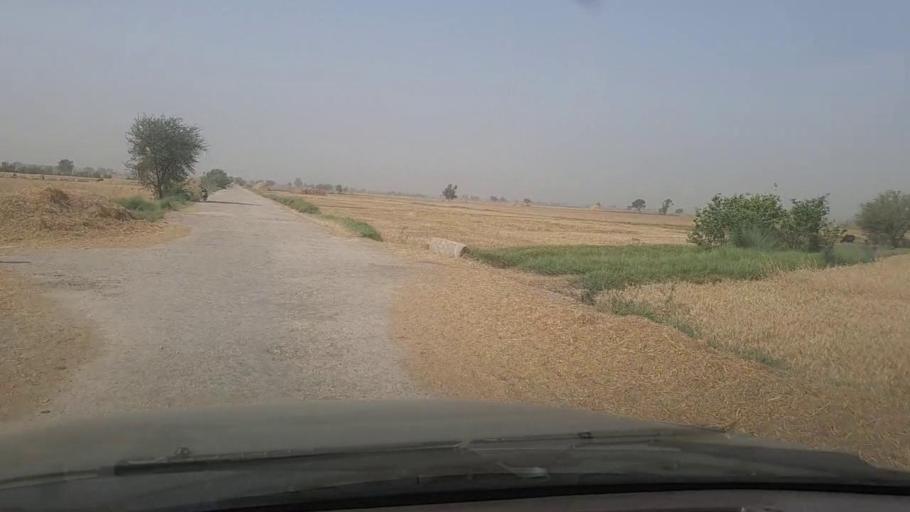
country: PK
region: Sindh
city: Garhi Yasin
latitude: 27.8933
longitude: 68.5829
